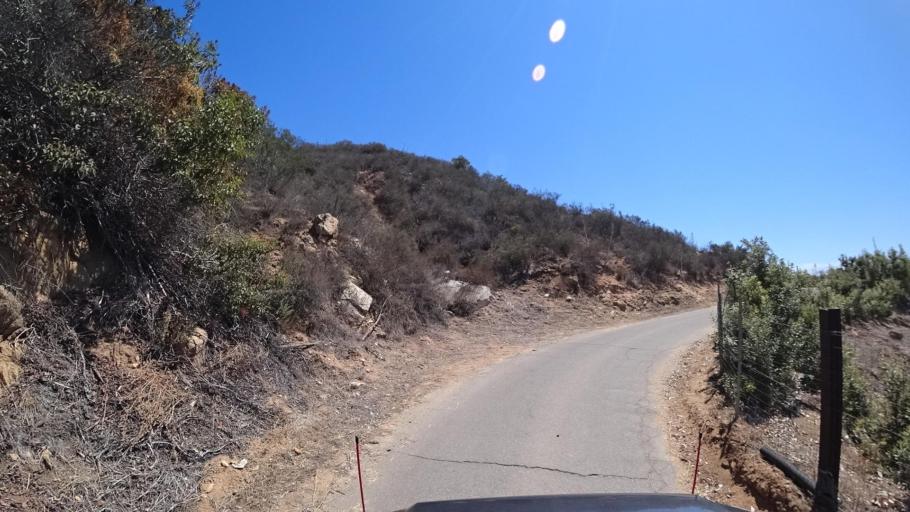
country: US
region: California
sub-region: San Diego County
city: Rainbow
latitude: 33.3870
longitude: -117.1012
